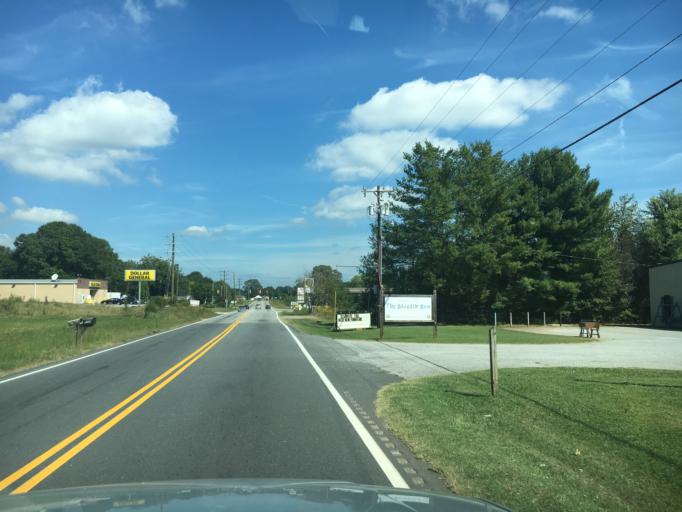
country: US
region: South Carolina
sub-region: Spartanburg County
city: Boiling Springs
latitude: 35.0543
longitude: -81.9383
